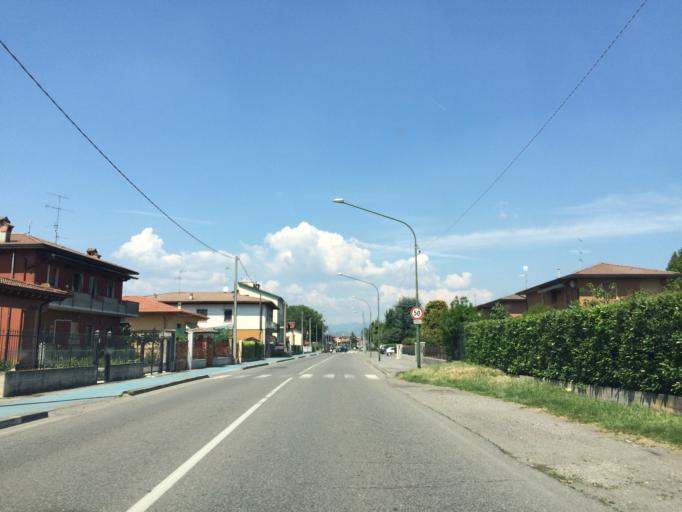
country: IT
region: Lombardy
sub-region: Provincia di Brescia
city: Flero
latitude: 45.4797
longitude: 10.1784
